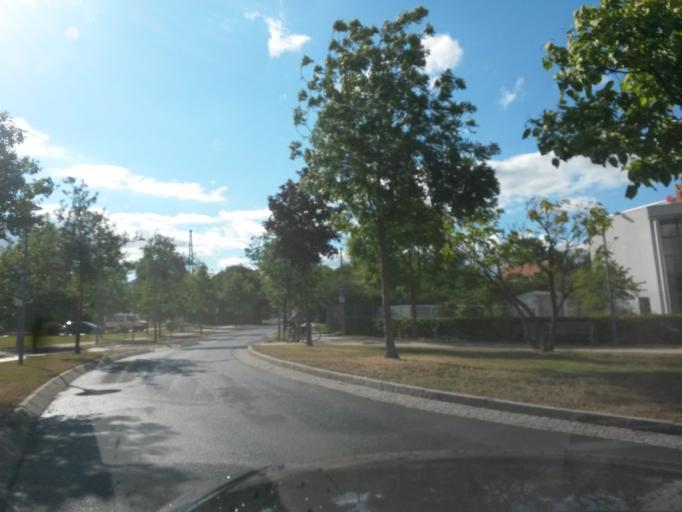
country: DE
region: Bavaria
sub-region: Regierungsbezirk Unterfranken
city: Rottendorf
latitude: 49.7895
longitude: 10.0308
